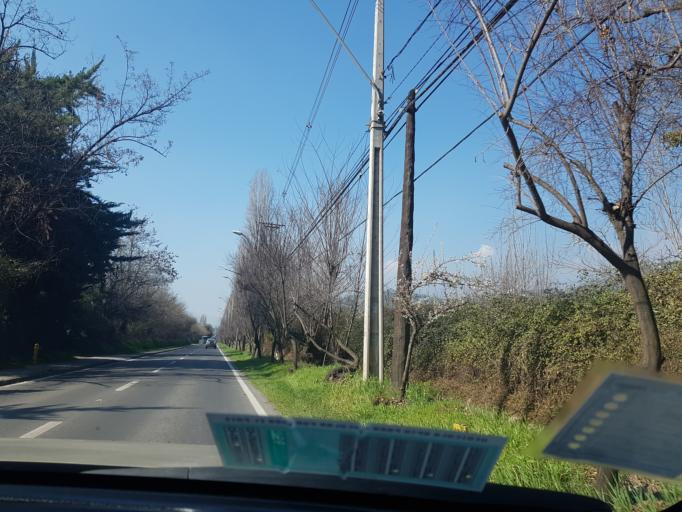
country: CL
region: Santiago Metropolitan
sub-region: Provincia de Cordillera
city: Puente Alto
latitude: -33.6317
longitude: -70.5629
